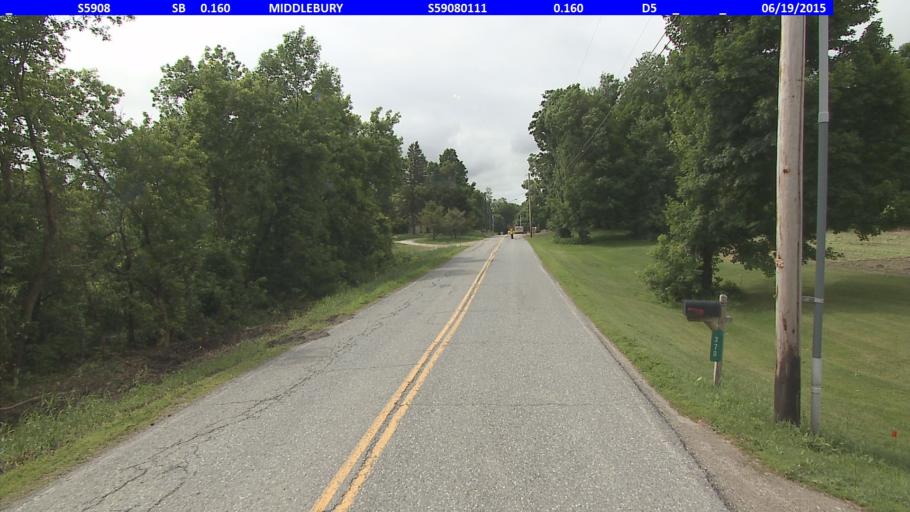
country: US
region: Vermont
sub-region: Addison County
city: Middlebury (village)
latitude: 43.9978
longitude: -73.1344
